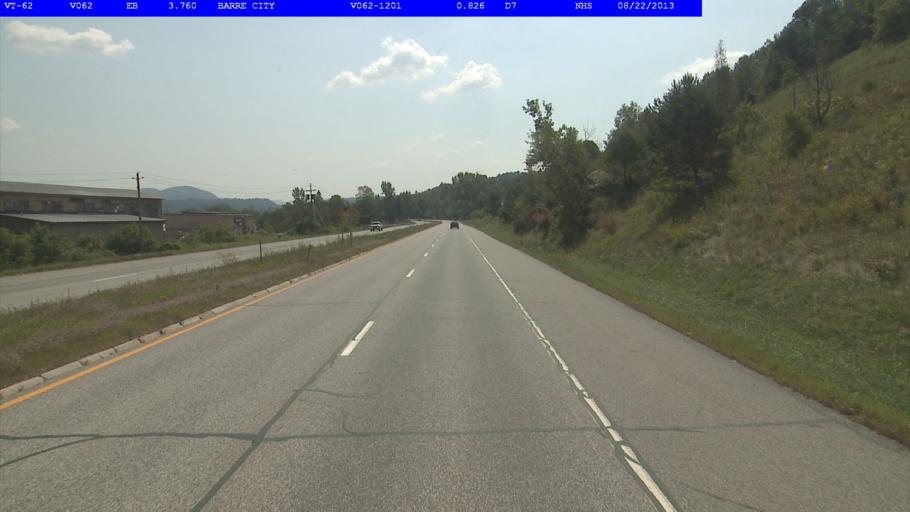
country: US
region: Vermont
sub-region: Washington County
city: Barre
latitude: 44.2078
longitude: -72.5197
